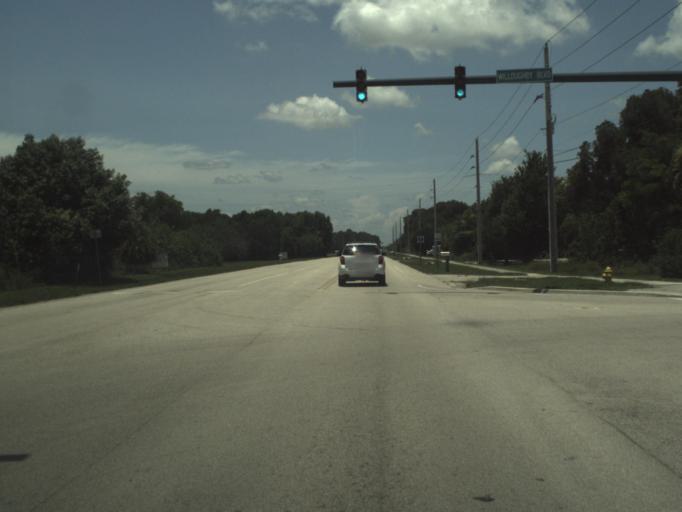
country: US
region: Florida
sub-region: Martin County
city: Port Salerno
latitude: 27.1278
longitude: -80.2226
